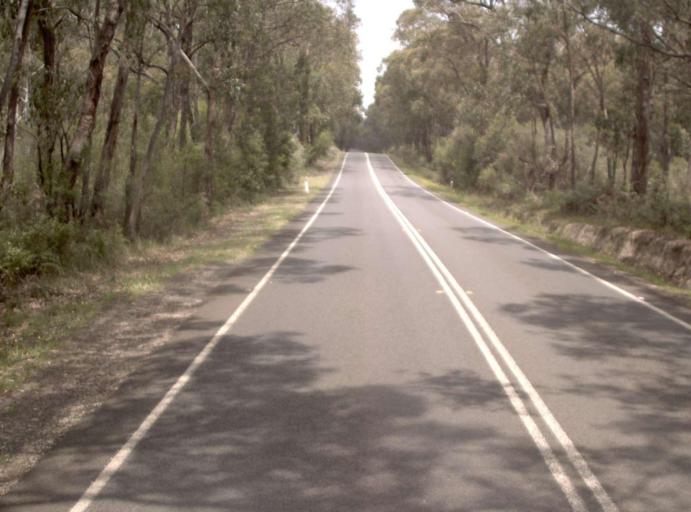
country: AU
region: Victoria
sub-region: Latrobe
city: Traralgon
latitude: -38.4119
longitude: 146.7497
